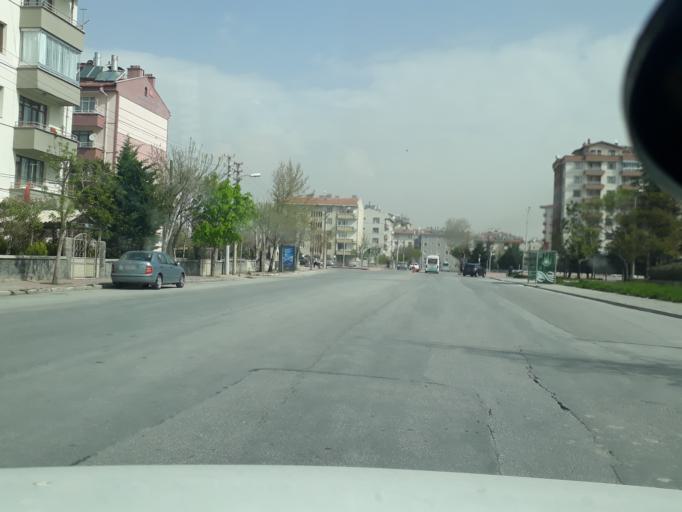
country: TR
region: Konya
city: Selcuklu
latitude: 37.9360
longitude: 32.4990
